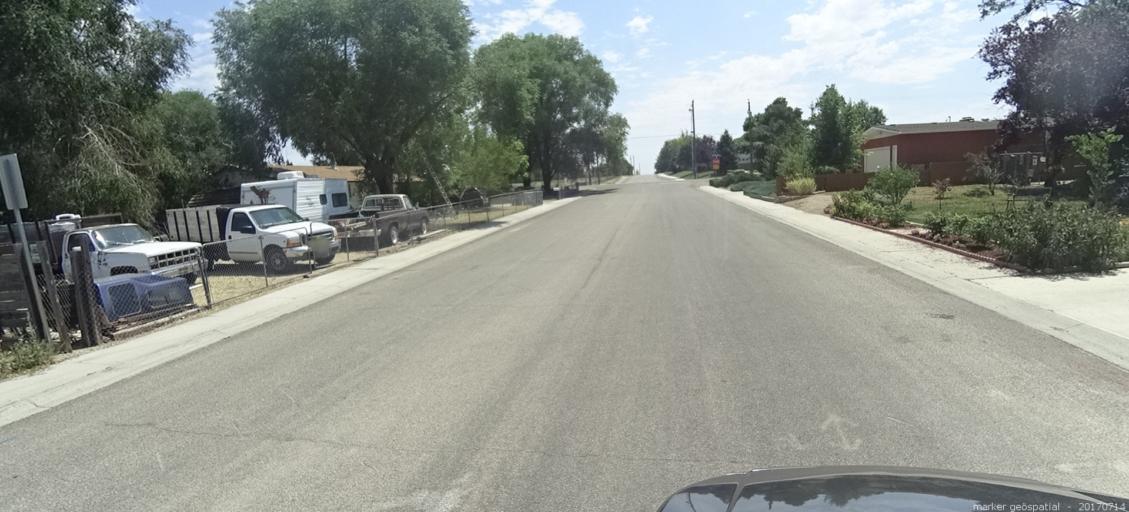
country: US
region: Idaho
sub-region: Ada County
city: Meridian
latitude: 43.5327
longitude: -116.3245
